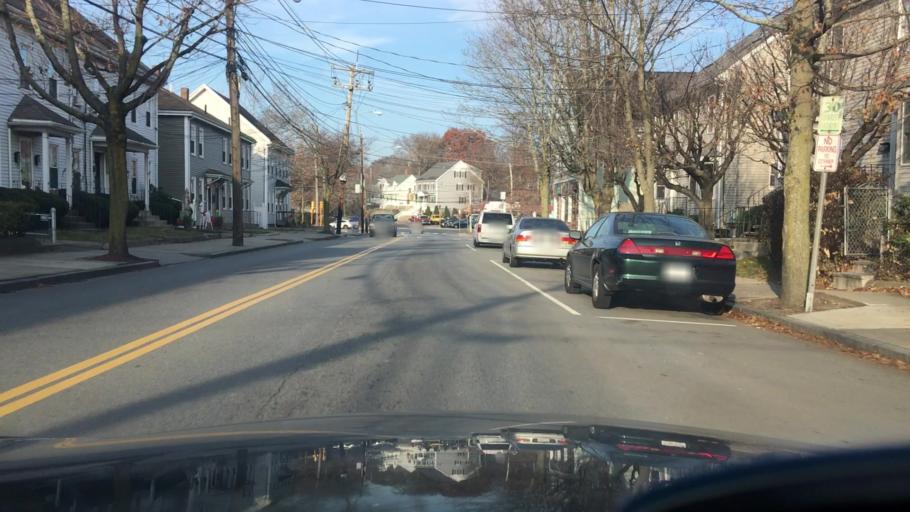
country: US
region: Massachusetts
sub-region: Middlesex County
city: Waltham
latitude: 42.3728
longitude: -71.2270
